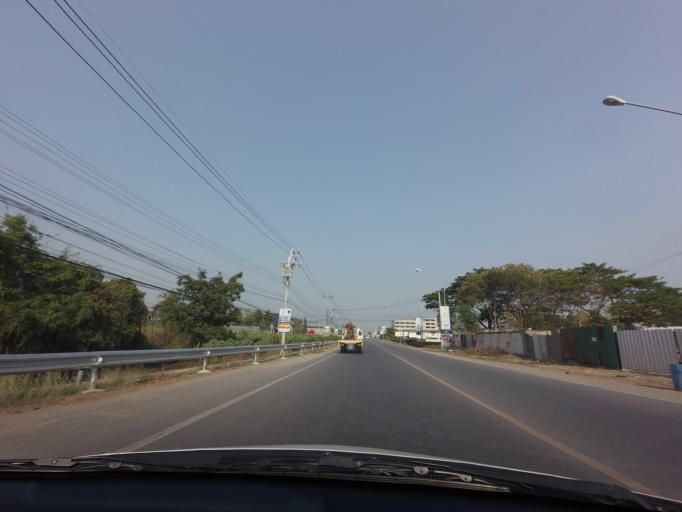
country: TH
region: Nakhon Pathom
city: Salaya
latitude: 13.8115
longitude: 100.3402
